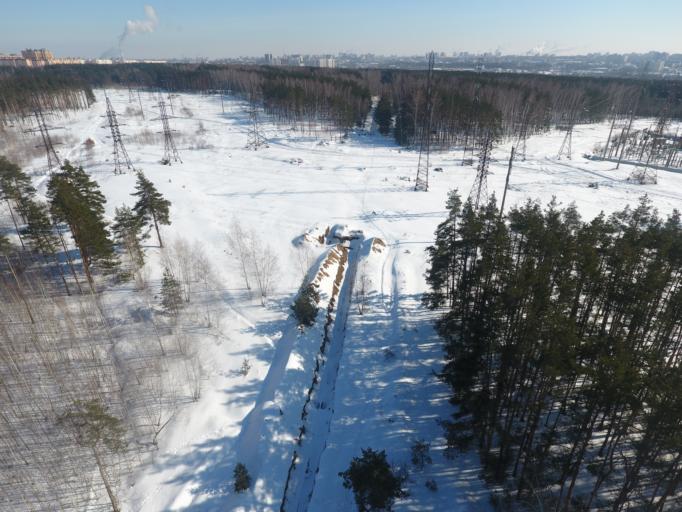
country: RU
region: Voronezj
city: Pridonskoy
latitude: 51.6750
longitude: 39.1034
